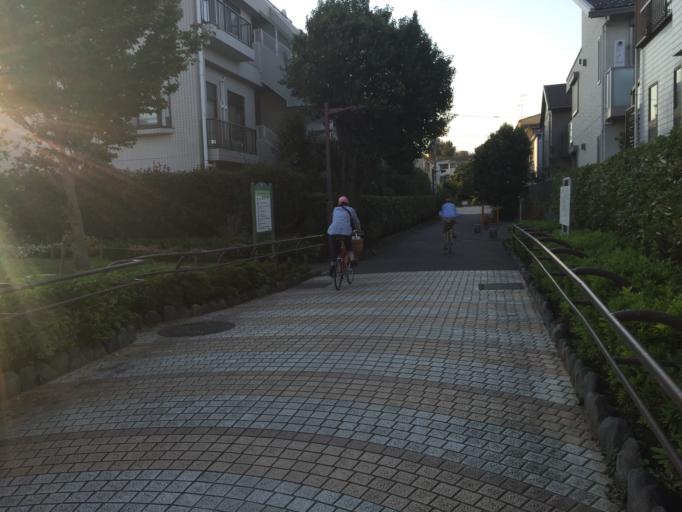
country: JP
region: Tokyo
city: Tokyo
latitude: 35.6469
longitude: 139.6635
